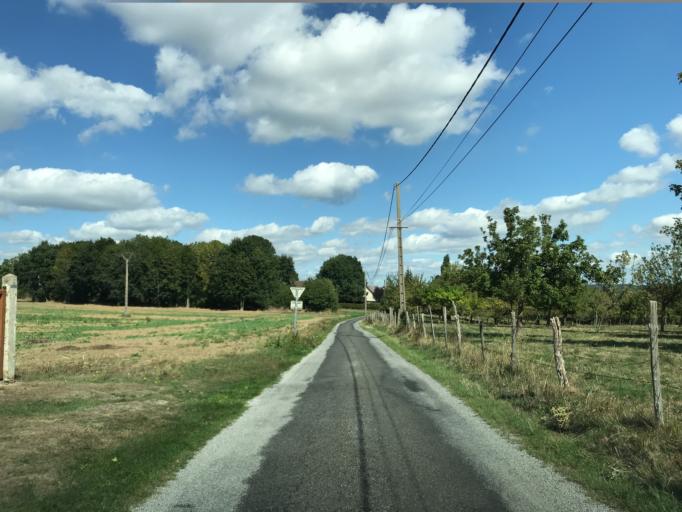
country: FR
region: Haute-Normandie
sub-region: Departement de l'Eure
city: La Chapelle-Reanville
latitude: 49.1350
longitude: 1.3951
